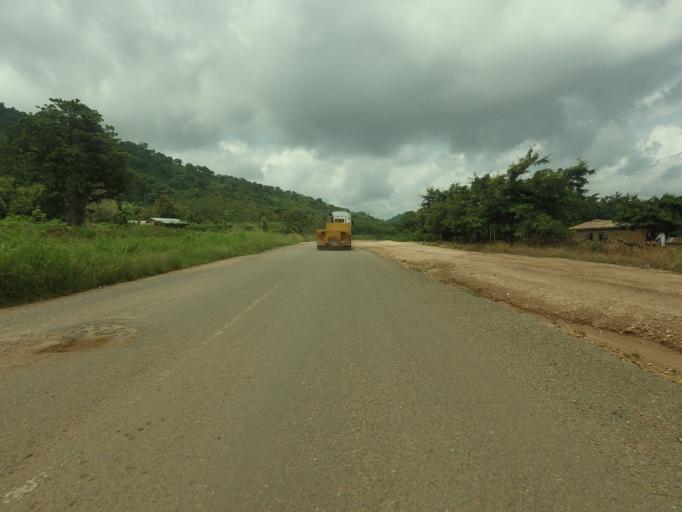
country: GH
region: Volta
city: Ho
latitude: 6.7034
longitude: 0.3346
